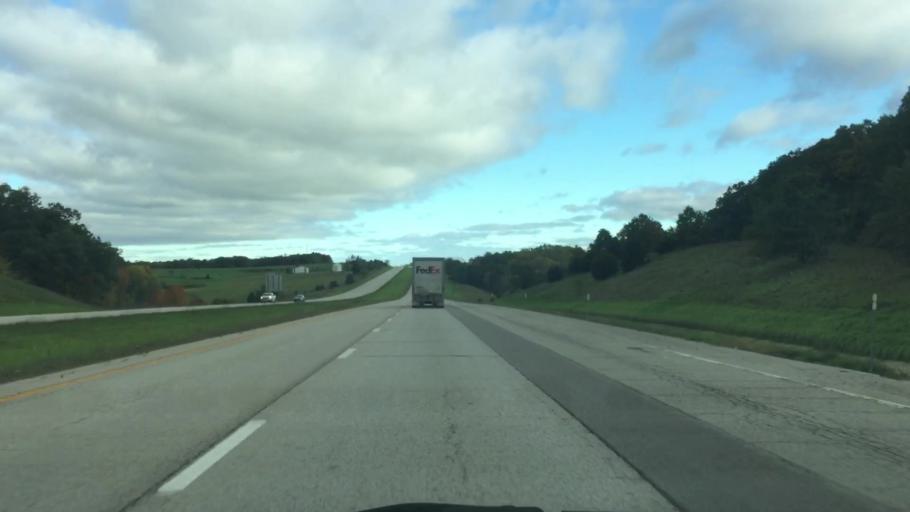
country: US
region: Missouri
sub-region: Harrison County
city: Bethany
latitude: 40.2141
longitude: -94.0132
